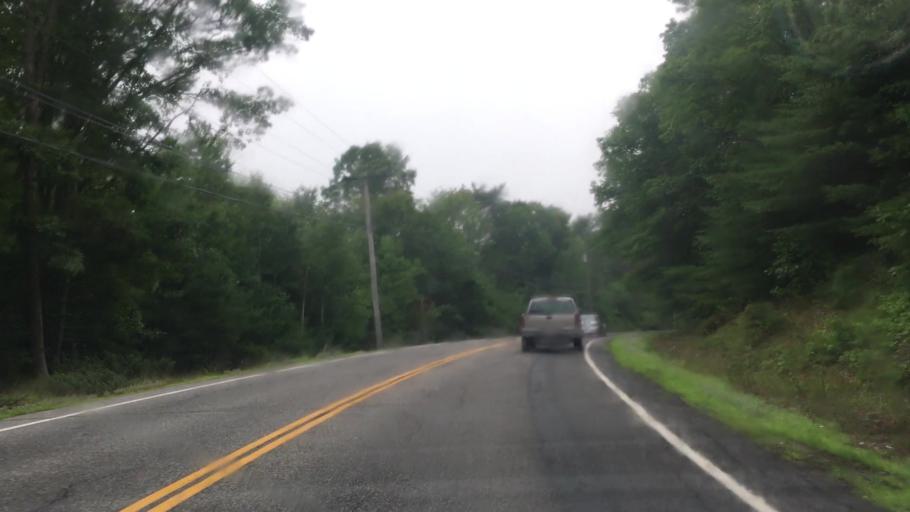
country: US
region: Maine
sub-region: Lincoln County
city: Wiscasset
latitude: 43.9983
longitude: -69.6322
